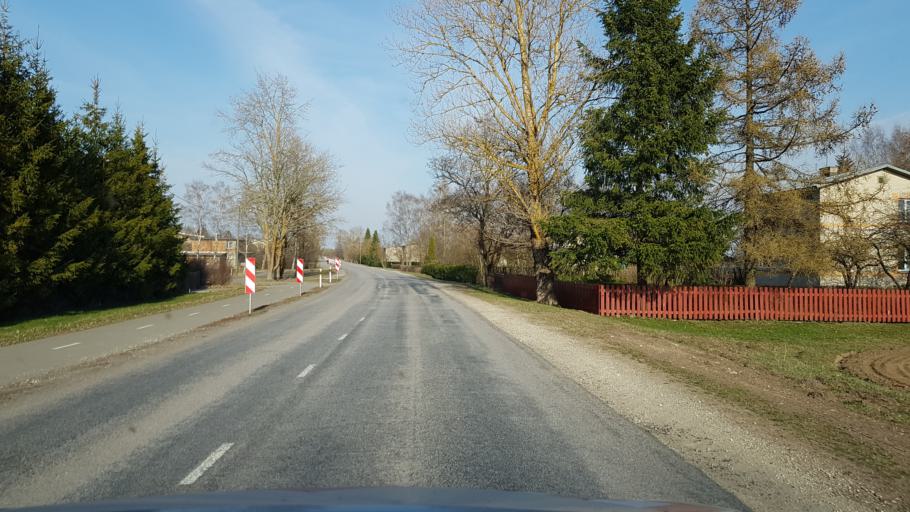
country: EE
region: Laeaene-Virumaa
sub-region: Rakvere linn
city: Rakvere
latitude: 59.3312
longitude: 26.2995
